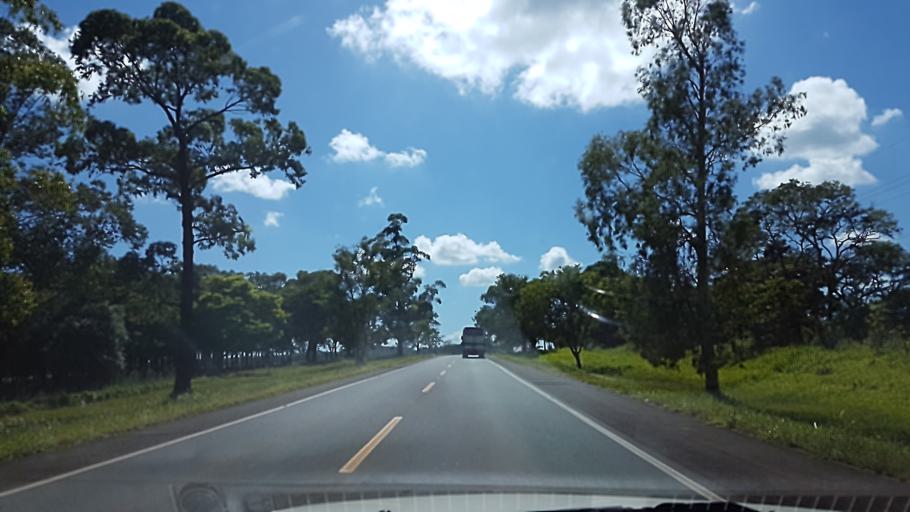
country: PY
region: Itapua
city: Carmen del Parana
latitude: -27.2211
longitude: -56.1114
